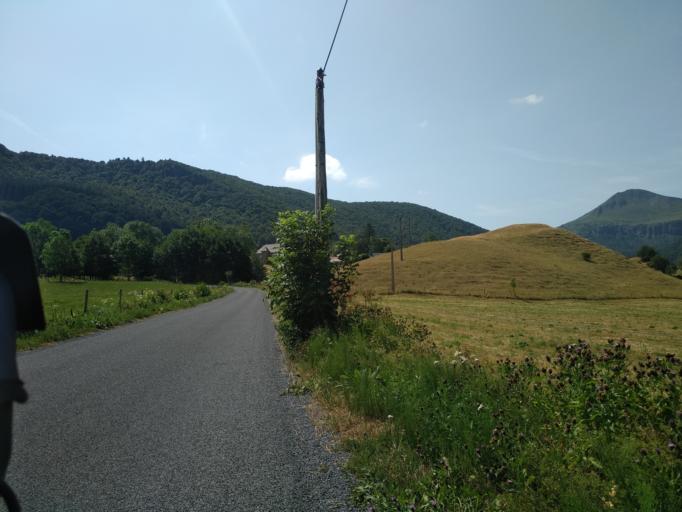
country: FR
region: Auvergne
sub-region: Departement du Cantal
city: Riom-es-Montagnes
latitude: 45.1392
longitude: 2.6971
